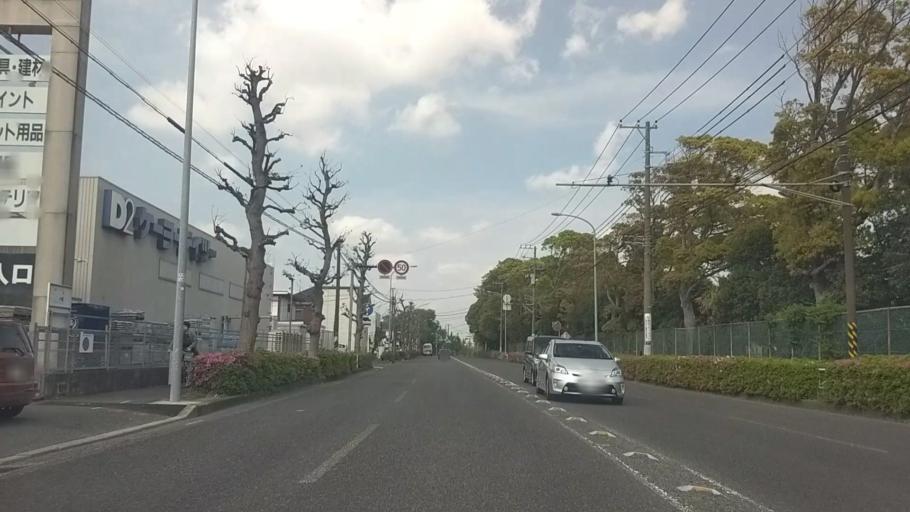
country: JP
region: Kanagawa
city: Yokohama
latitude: 35.3858
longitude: 139.5908
